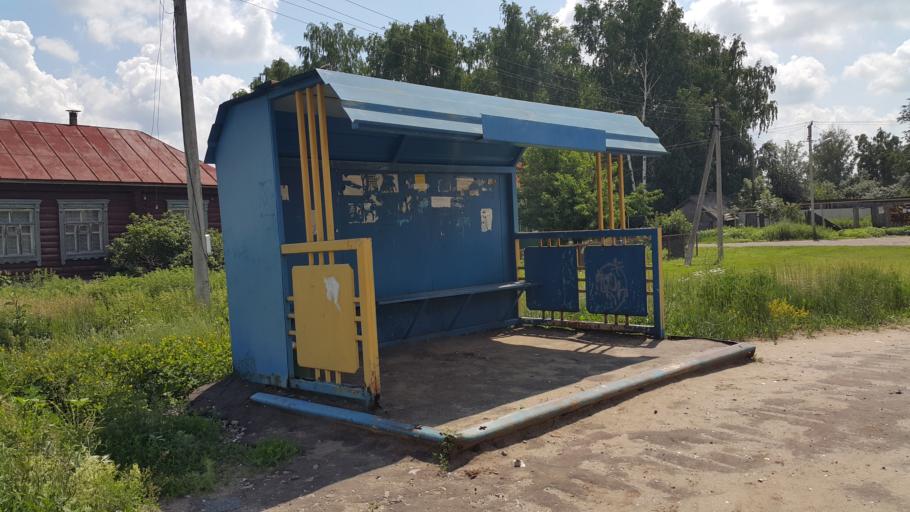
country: RU
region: Tambov
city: Morshansk
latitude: 53.6199
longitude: 41.8508
